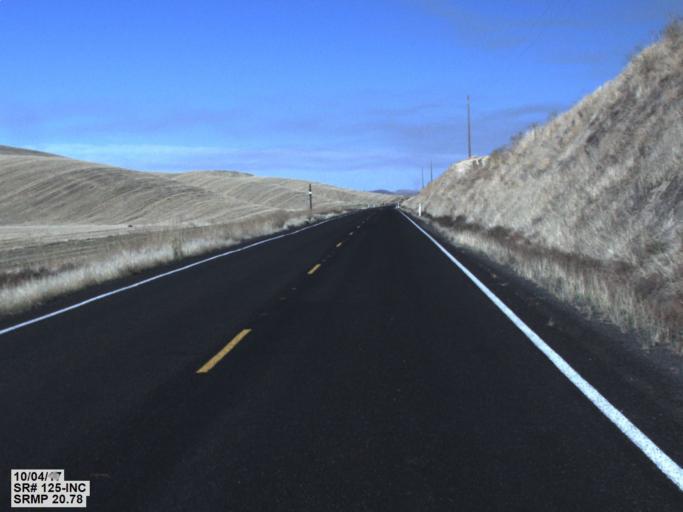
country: US
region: Washington
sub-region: Walla Walla County
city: Walla Walla
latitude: 46.2592
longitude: -118.3553
